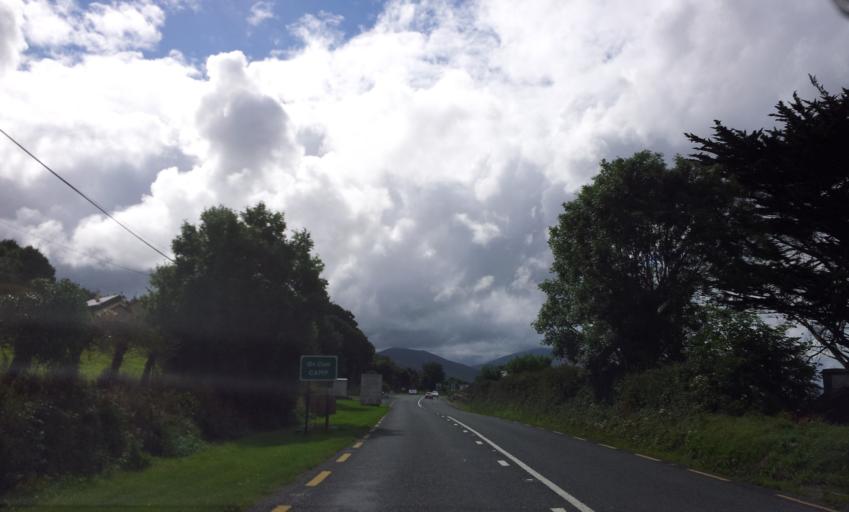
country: IE
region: Munster
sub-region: Ciarrai
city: Killorglin
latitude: 52.2267
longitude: -9.8895
